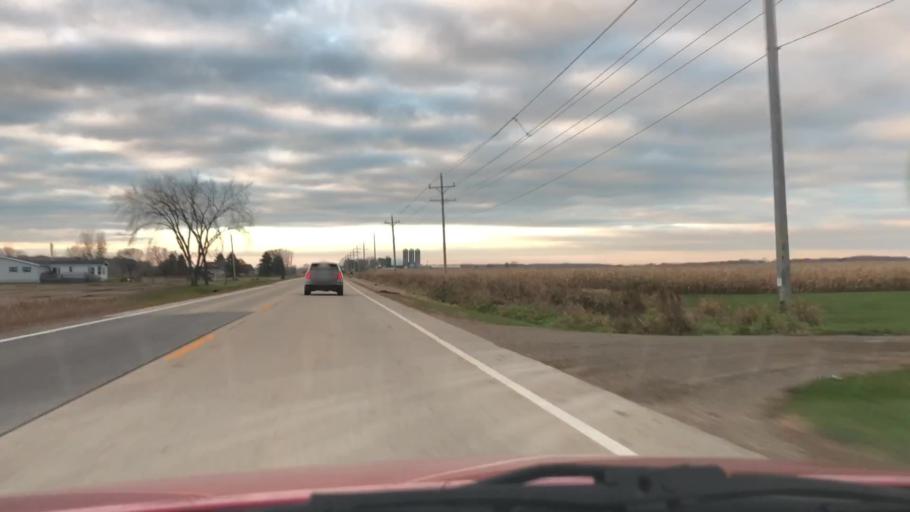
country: US
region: Wisconsin
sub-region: Outagamie County
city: Seymour
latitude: 44.4502
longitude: -88.2913
